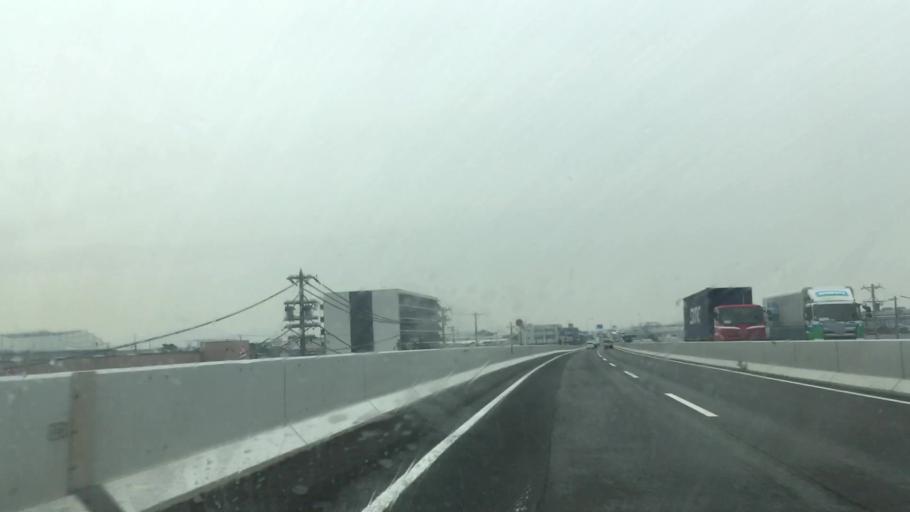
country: JP
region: Aichi
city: Anjo
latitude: 34.9224
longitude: 137.0548
